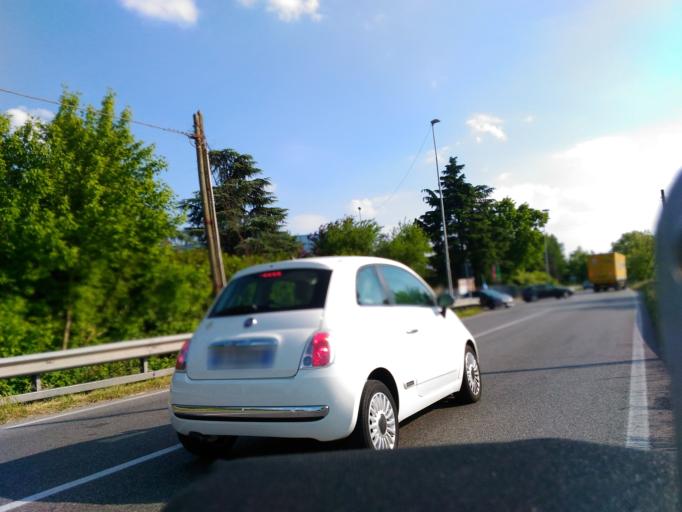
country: IT
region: Lombardy
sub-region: Citta metropolitana di Milano
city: Mombretto
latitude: 45.4024
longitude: 9.3553
